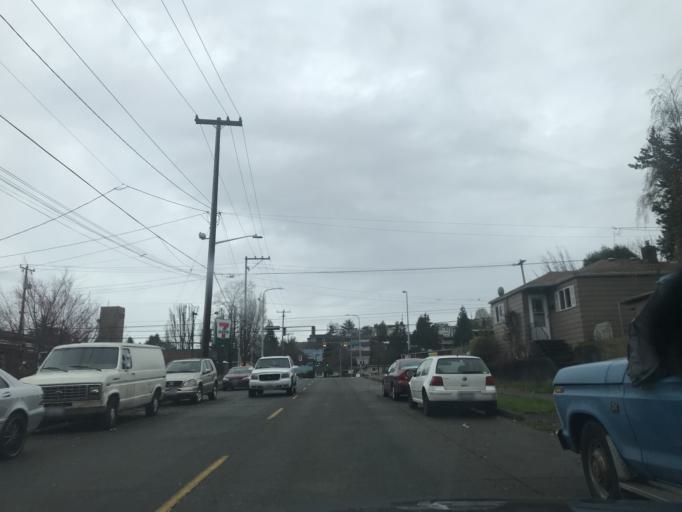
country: US
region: Washington
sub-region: King County
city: White Center
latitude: 47.5337
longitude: -122.3563
